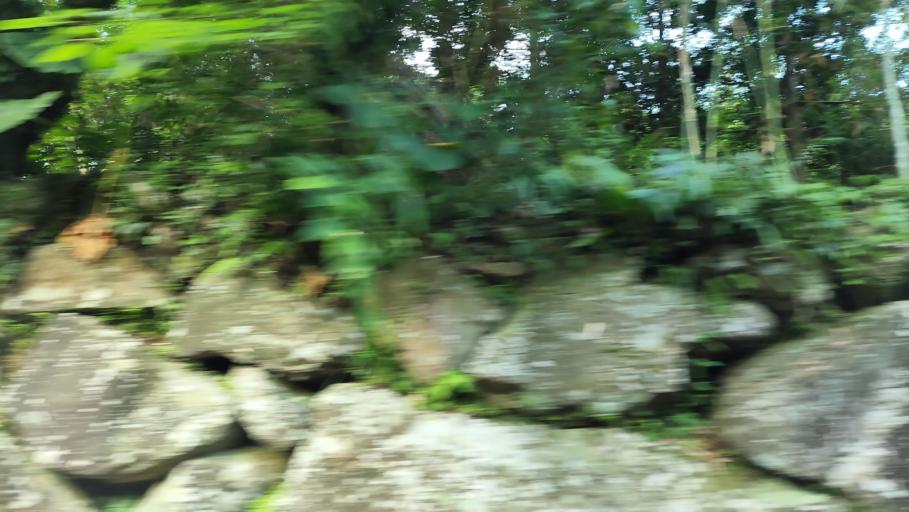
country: TW
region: Taiwan
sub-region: Keelung
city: Keelung
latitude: 25.1852
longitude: 121.6402
